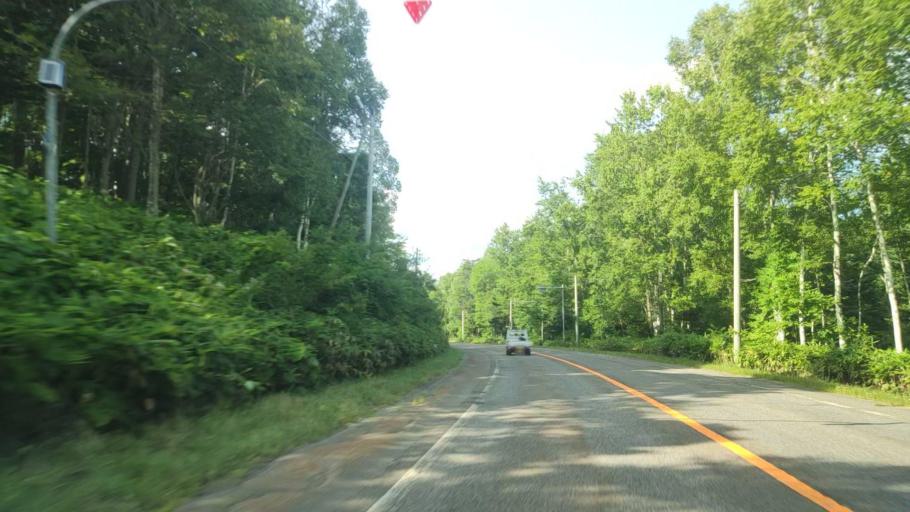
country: JP
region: Hokkaido
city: Nayoro
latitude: 44.3891
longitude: 142.3977
